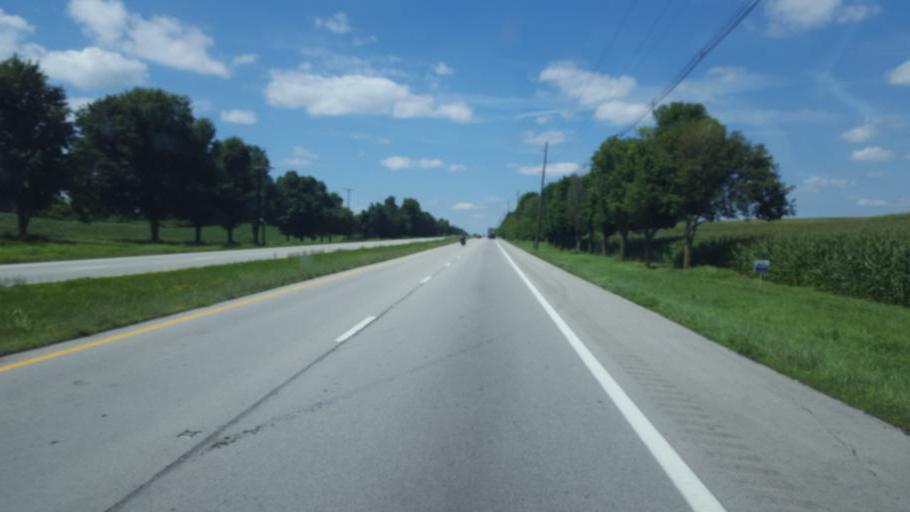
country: US
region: Ohio
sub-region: Franklin County
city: Obetz
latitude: 39.8466
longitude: -83.0016
